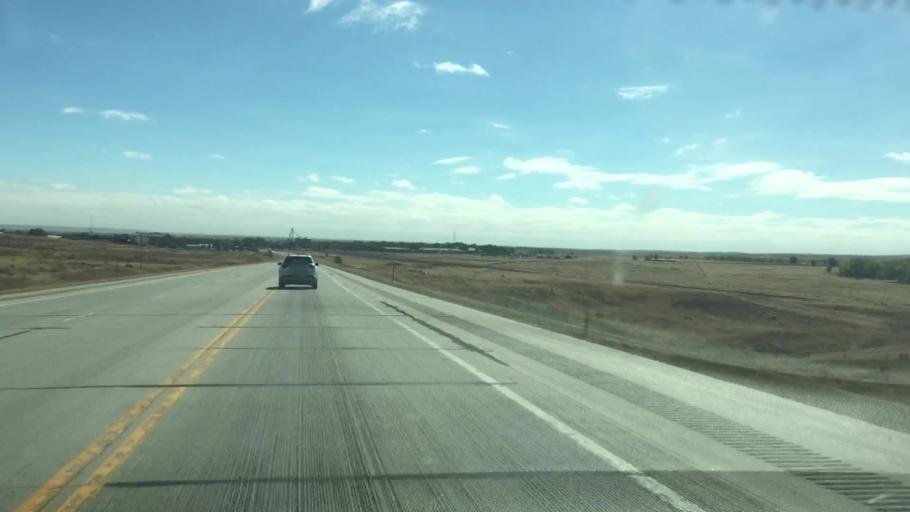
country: US
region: Colorado
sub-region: Lincoln County
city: Hugo
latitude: 39.1415
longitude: -103.4881
